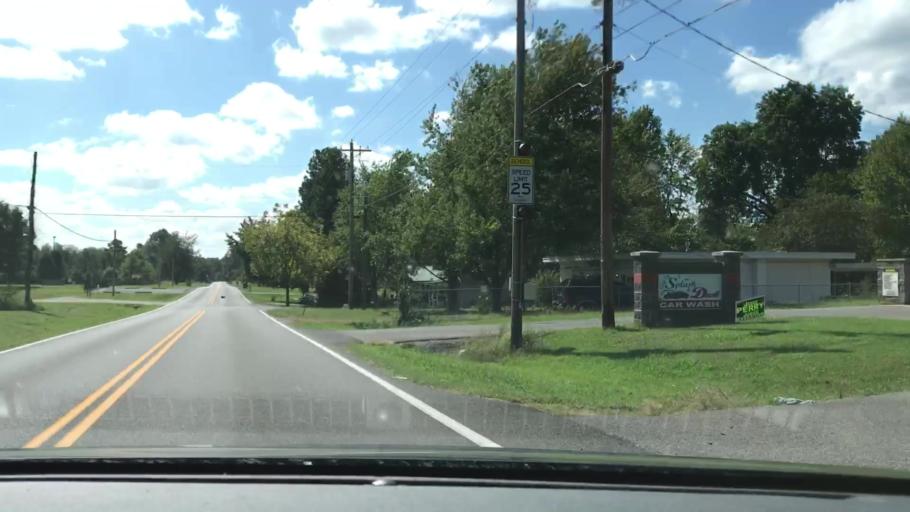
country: US
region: Kentucky
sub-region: McCracken County
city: Reidland
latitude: 36.9182
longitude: -88.5204
